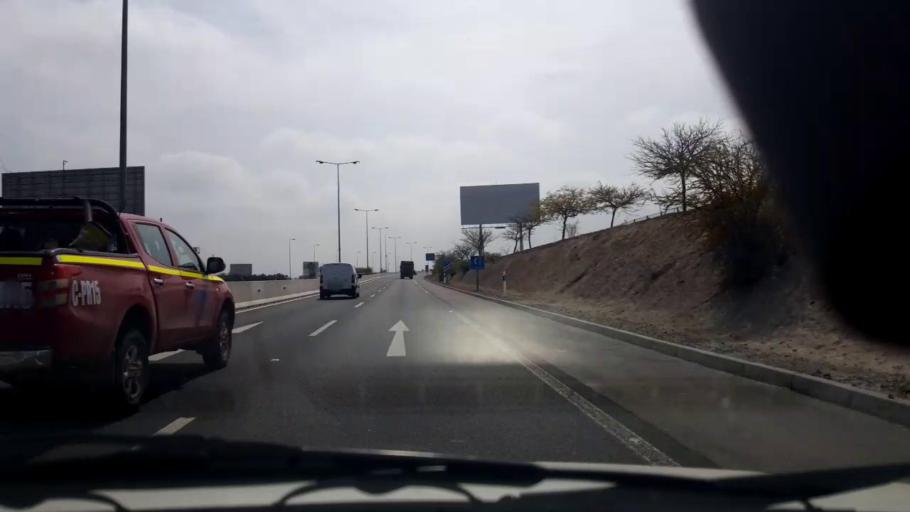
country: CL
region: Santiago Metropolitan
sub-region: Provincia de Santiago
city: Lo Prado
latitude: -33.4216
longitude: -70.7957
